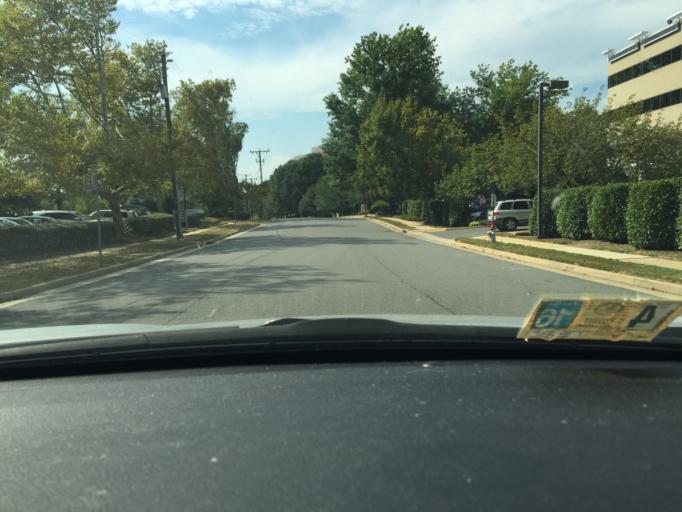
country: US
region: Virginia
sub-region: Fairfax County
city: Tysons Corner
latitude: 38.9155
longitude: -77.2301
